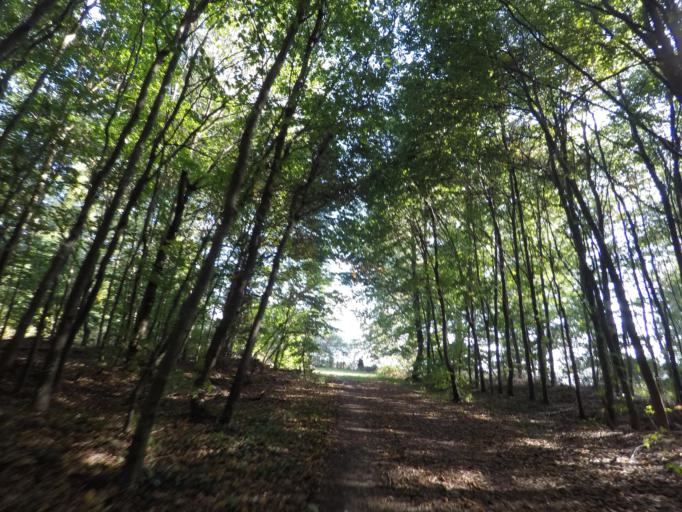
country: LU
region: Luxembourg
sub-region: Canton de Luxembourg
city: Hesperange
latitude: 49.5845
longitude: 6.1536
